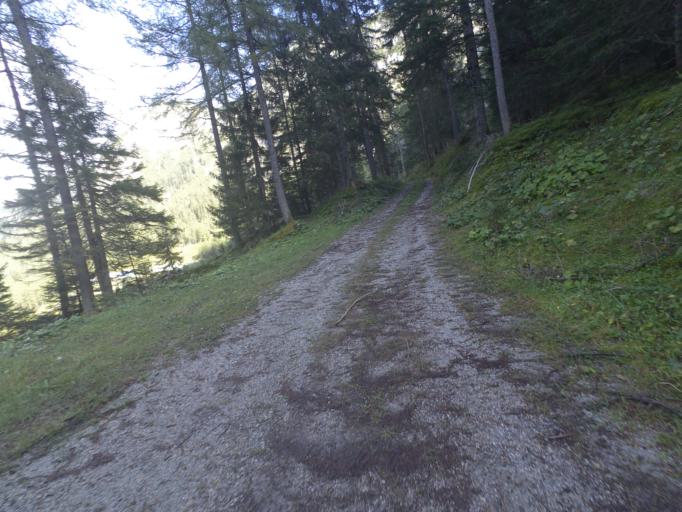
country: AT
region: Salzburg
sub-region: Politischer Bezirk Sankt Johann im Pongau
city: Untertauern
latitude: 47.2374
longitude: 13.4206
